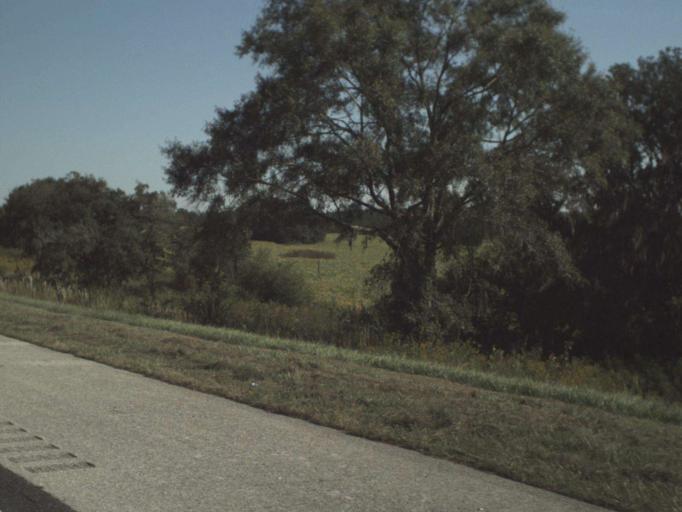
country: US
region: Florida
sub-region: Holmes County
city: Bonifay
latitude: 30.7601
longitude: -85.7552
